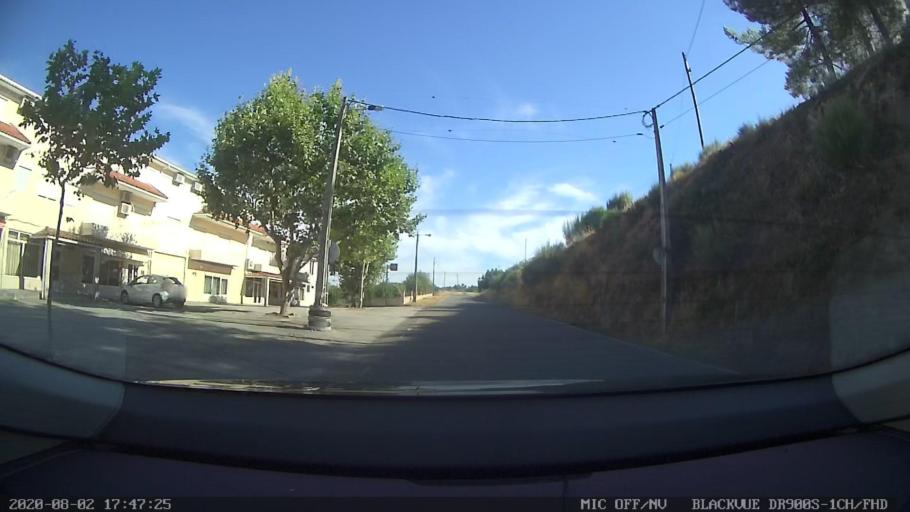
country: PT
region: Vila Real
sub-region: Murca
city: Murca
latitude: 41.4035
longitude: -7.4792
